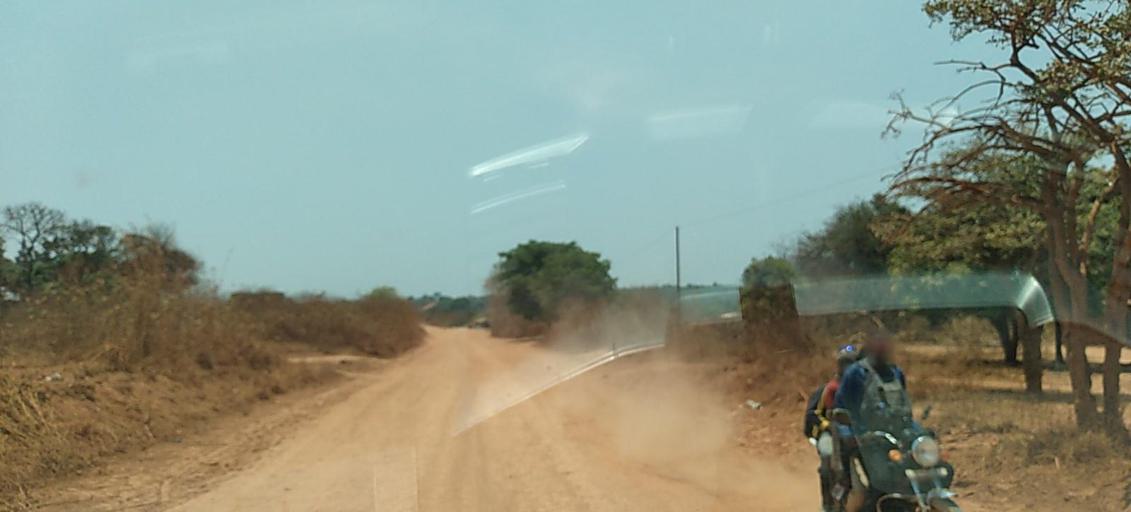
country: CD
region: Katanga
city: Kipushi
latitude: -11.7796
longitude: 27.1907
